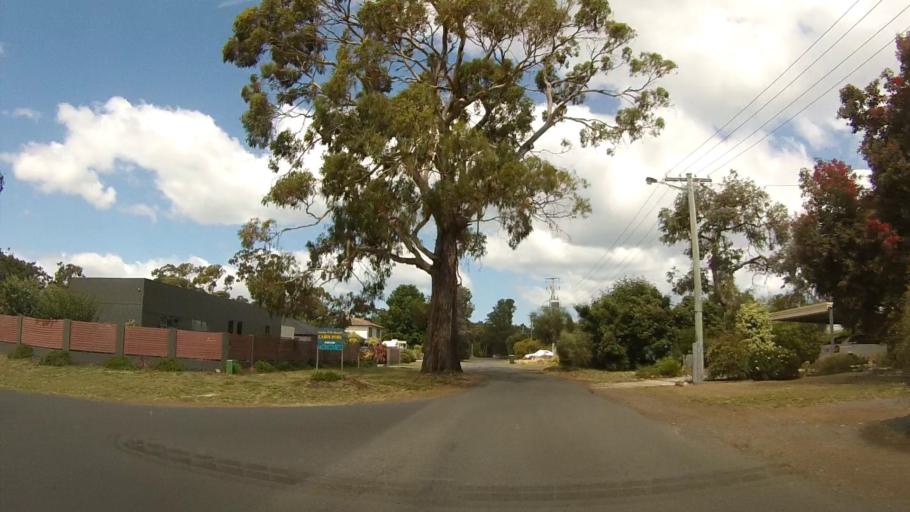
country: AU
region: Tasmania
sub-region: Clarence
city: Seven Mile Beach
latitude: -42.8553
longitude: 147.5069
